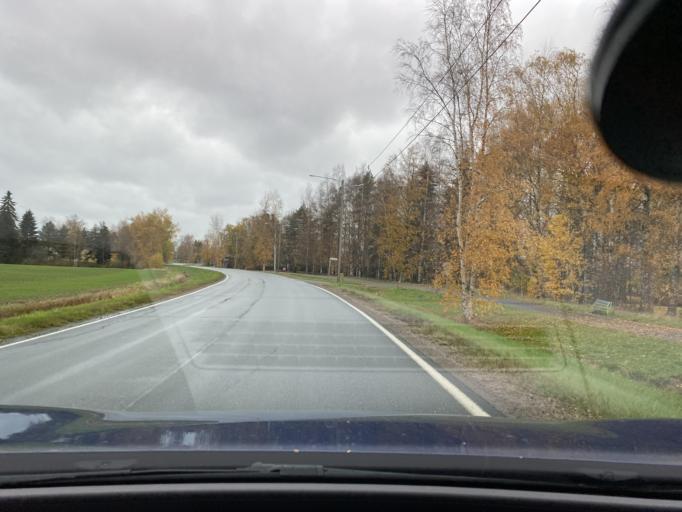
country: FI
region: Satakunta
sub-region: Pori
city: Kokemaeki
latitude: 61.2579
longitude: 22.3732
